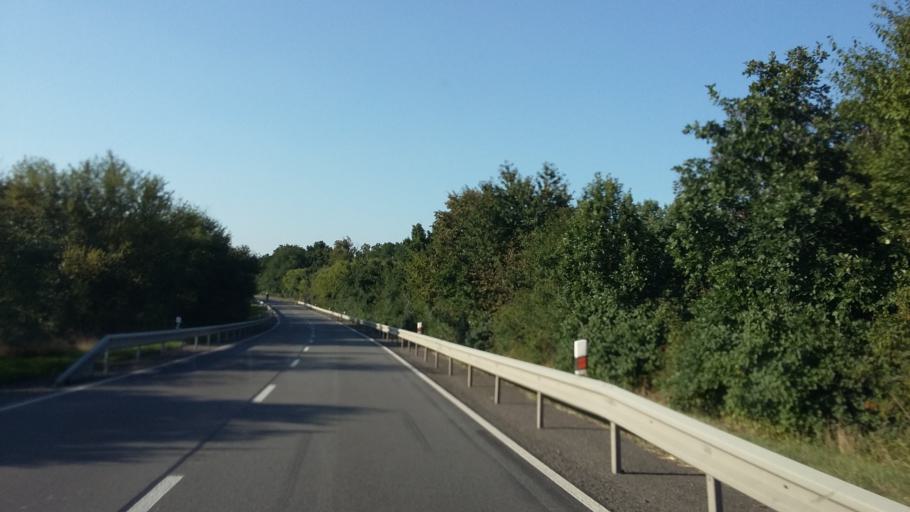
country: CZ
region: South Moravian
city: Ricany
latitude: 49.1965
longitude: 16.4243
